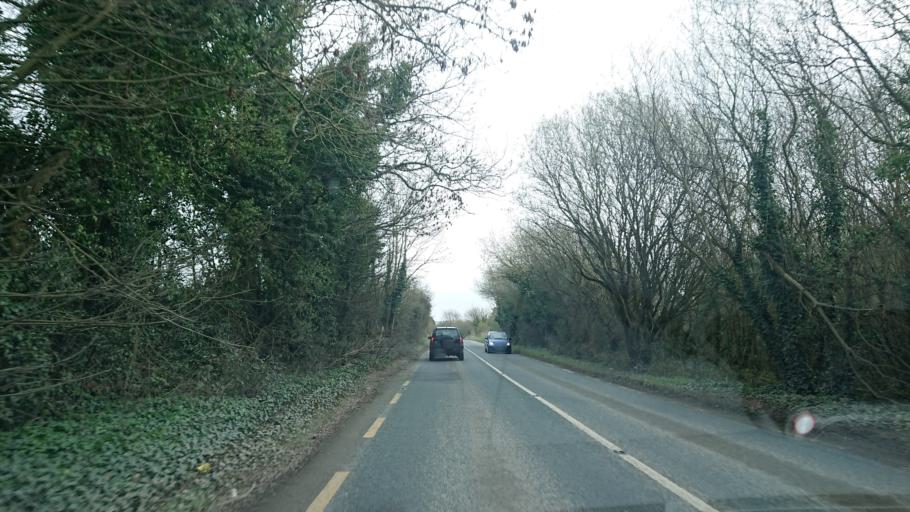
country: IE
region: Leinster
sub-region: Kildare
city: Johnstown
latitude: 53.2025
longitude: -6.6240
